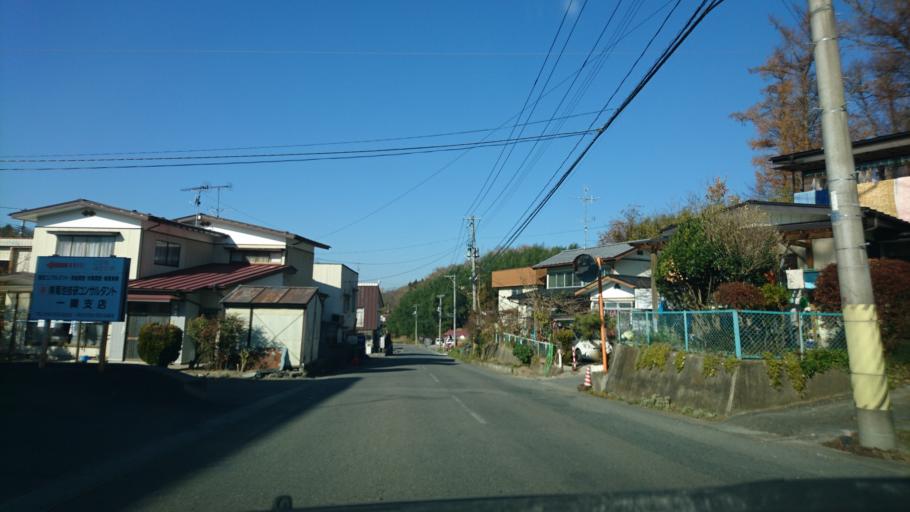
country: JP
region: Iwate
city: Ichinoseki
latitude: 38.9142
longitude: 141.3442
